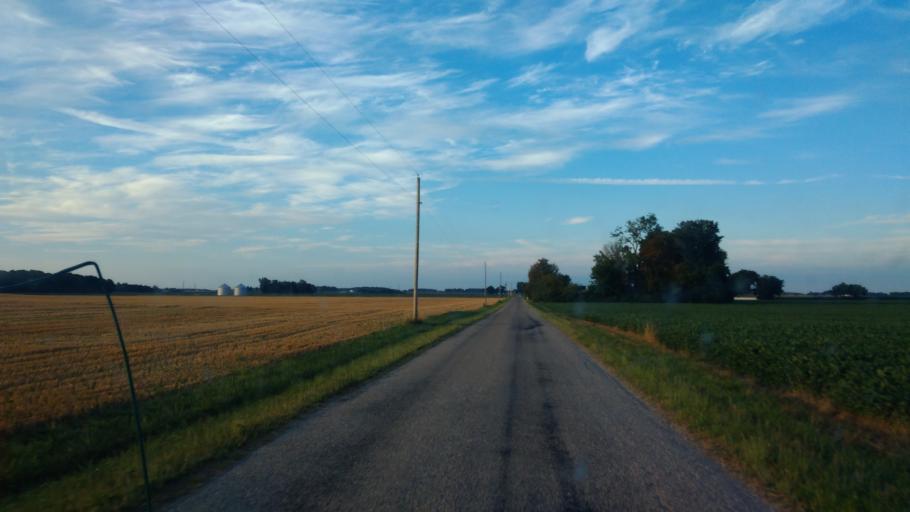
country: US
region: Indiana
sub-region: Adams County
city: Berne
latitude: 40.6455
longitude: -85.0607
